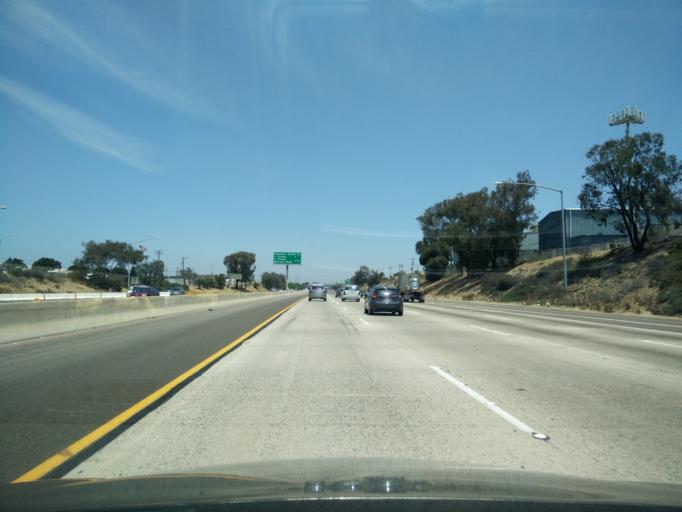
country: US
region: California
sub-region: San Diego County
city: Imperial Beach
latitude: 32.5970
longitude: -117.0891
